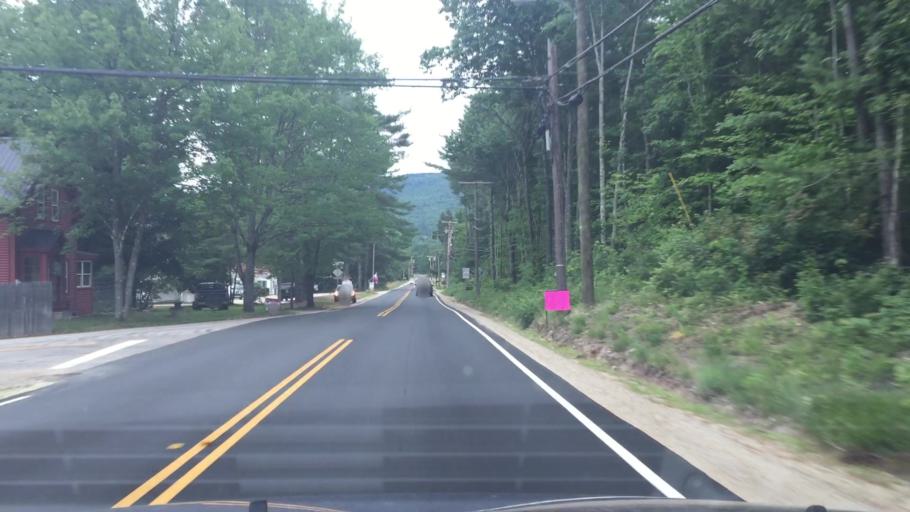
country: US
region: New Hampshire
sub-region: Carroll County
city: Freedom
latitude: 43.8019
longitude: -71.0590
